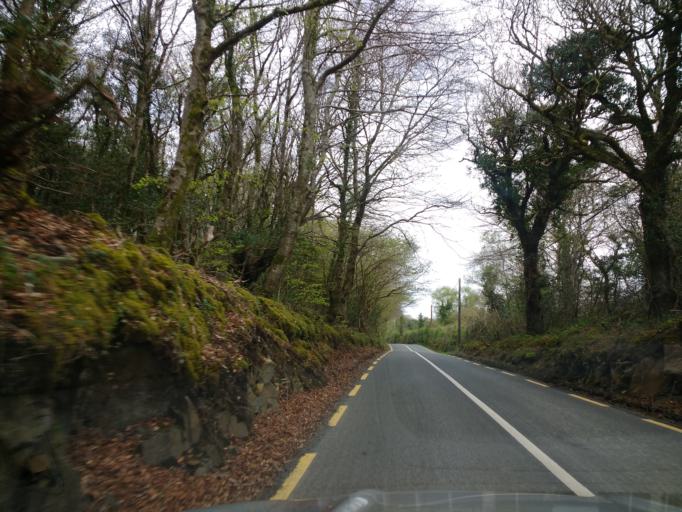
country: IE
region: Ulster
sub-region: County Donegal
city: Buncrana
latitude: 55.1291
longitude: -7.5287
